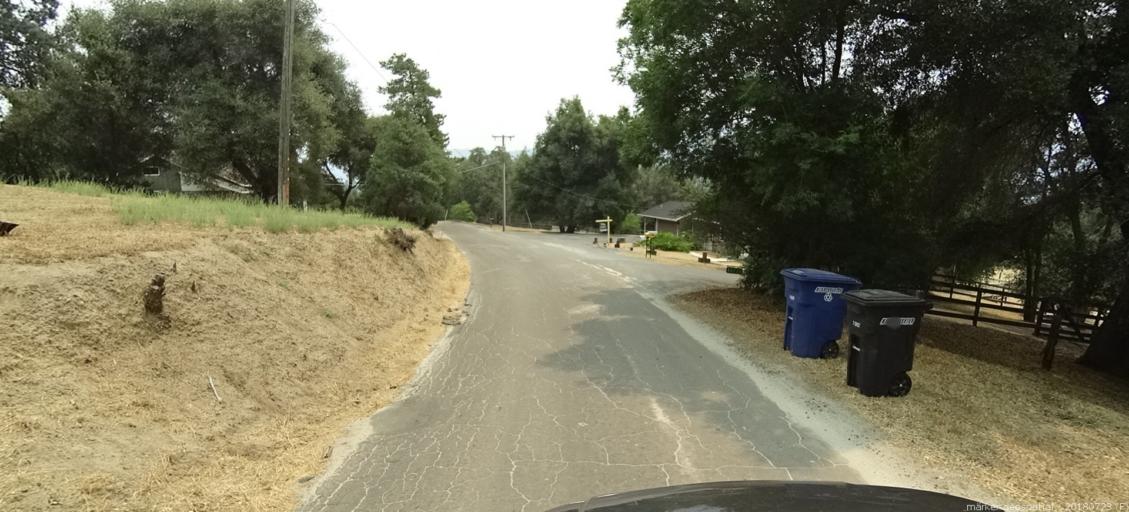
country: US
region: California
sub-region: Madera County
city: Oakhurst
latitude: 37.3398
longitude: -119.6520
